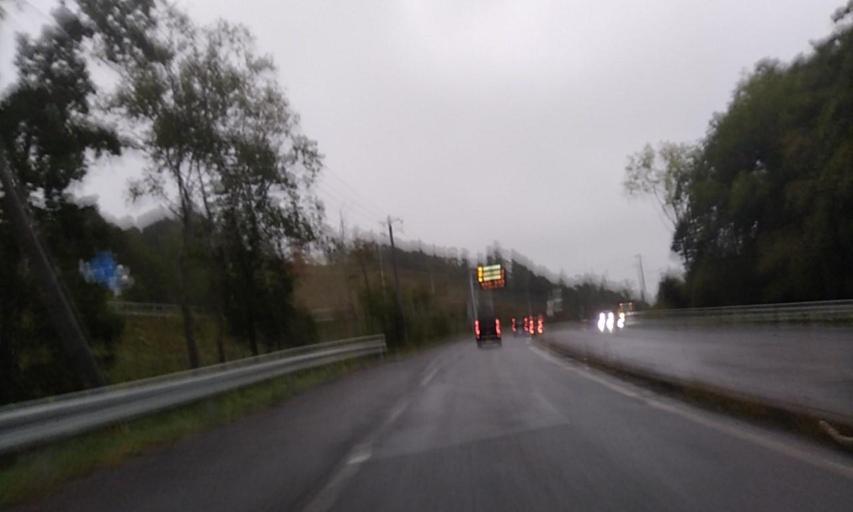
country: JP
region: Hokkaido
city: Kushiro
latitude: 43.0039
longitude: 144.5021
